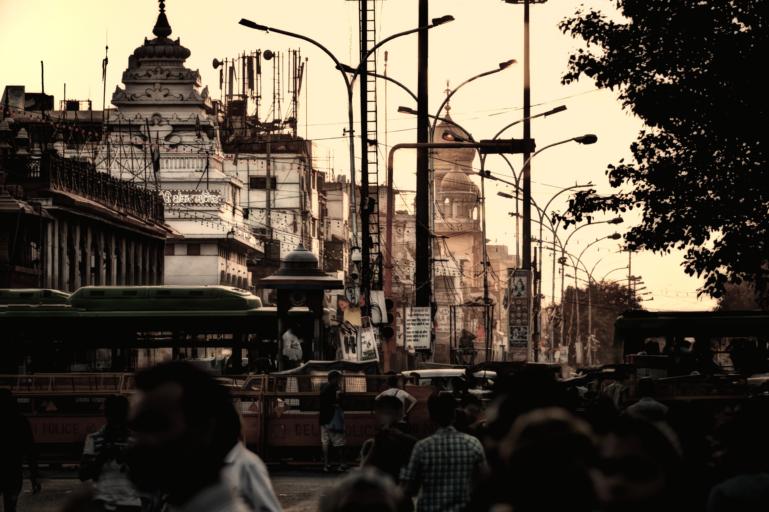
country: IN
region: NCT
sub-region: North Delhi
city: Delhi
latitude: 28.6561
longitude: 77.2379
